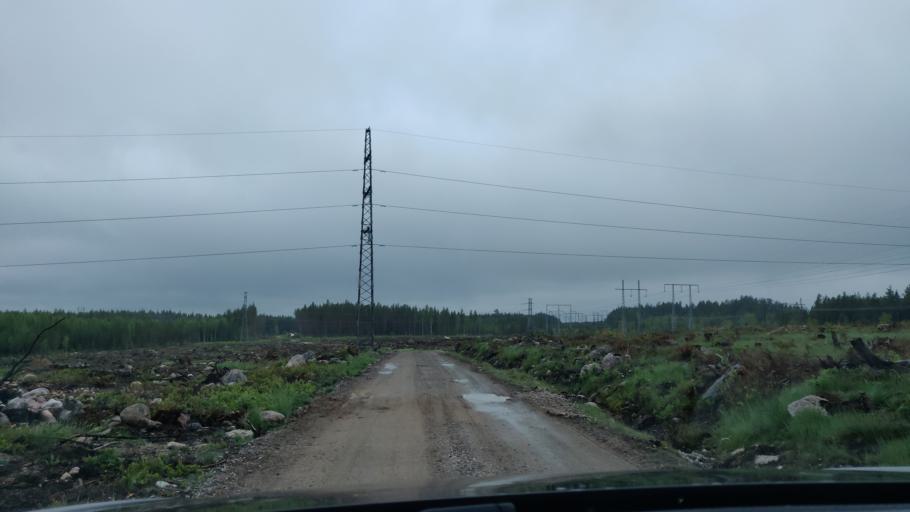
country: SE
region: Dalarna
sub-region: Avesta Kommun
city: Horndal
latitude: 60.3131
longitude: 16.4005
